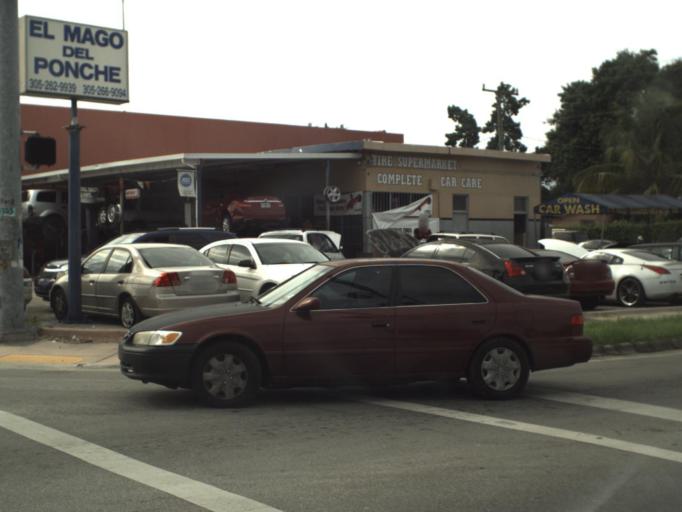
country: US
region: Florida
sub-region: Miami-Dade County
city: West Miami
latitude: 25.7634
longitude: -80.2959
